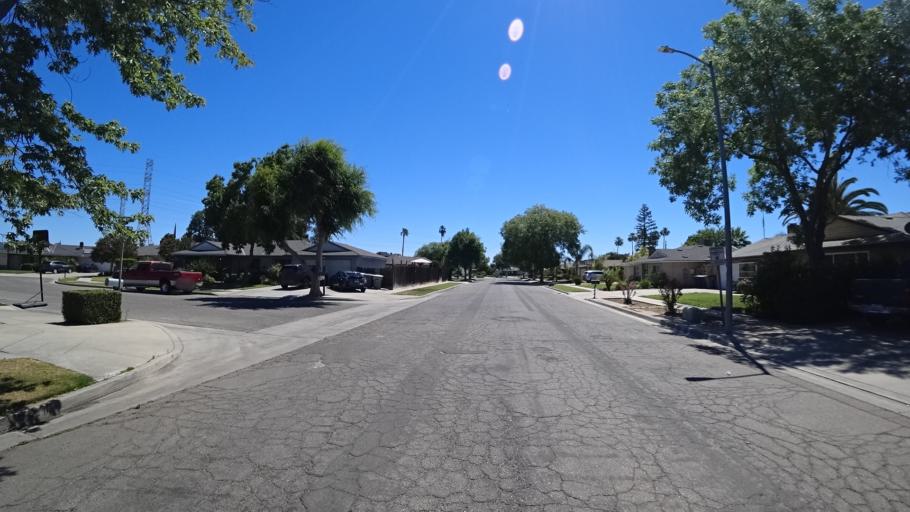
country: US
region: California
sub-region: Fresno County
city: West Park
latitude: 36.8017
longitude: -119.8477
